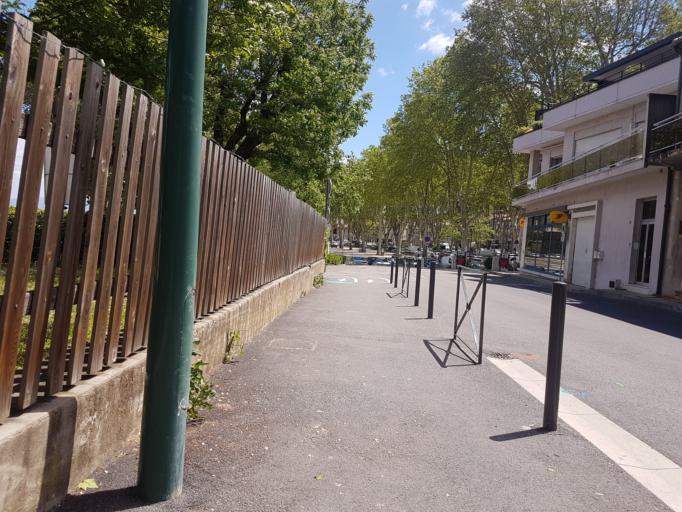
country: FR
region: Rhone-Alpes
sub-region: Departement de l'Ardeche
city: Tournon-sur-Rhone
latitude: 45.0712
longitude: 4.8280
